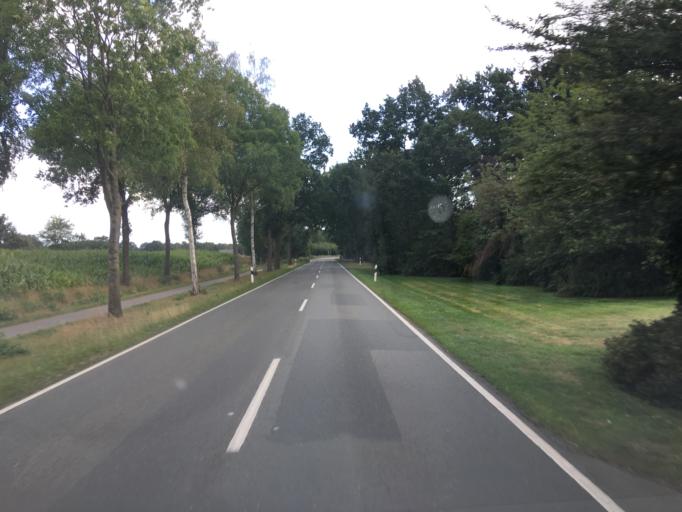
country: DE
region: Lower Saxony
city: Friesoythe
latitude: 53.0543
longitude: 7.8575
